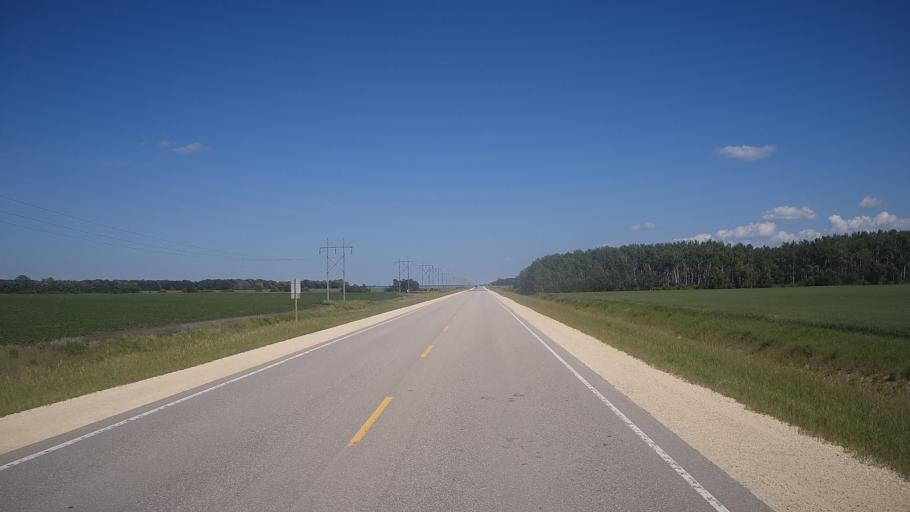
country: CA
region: Manitoba
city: Stonewall
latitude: 50.1227
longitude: -97.4550
